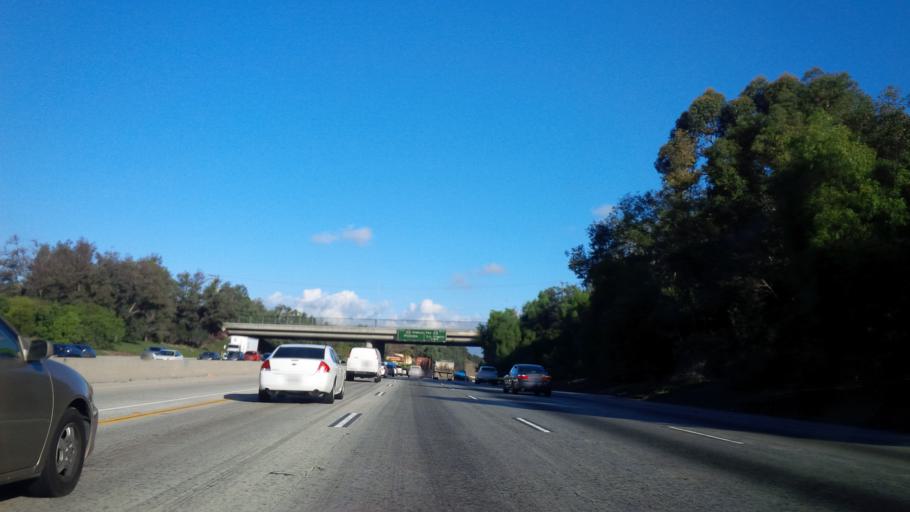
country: US
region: California
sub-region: Los Angeles County
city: Walnut
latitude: 33.9828
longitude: -117.8421
